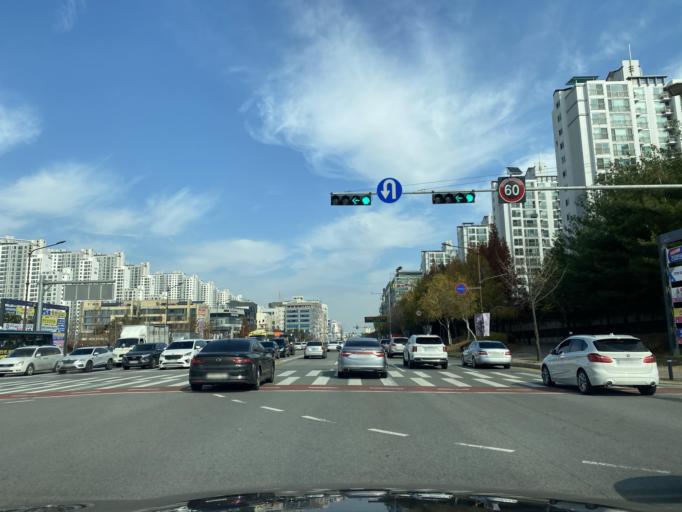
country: KR
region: Chungcheongnam-do
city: Cheonan
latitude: 36.8075
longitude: 127.1073
